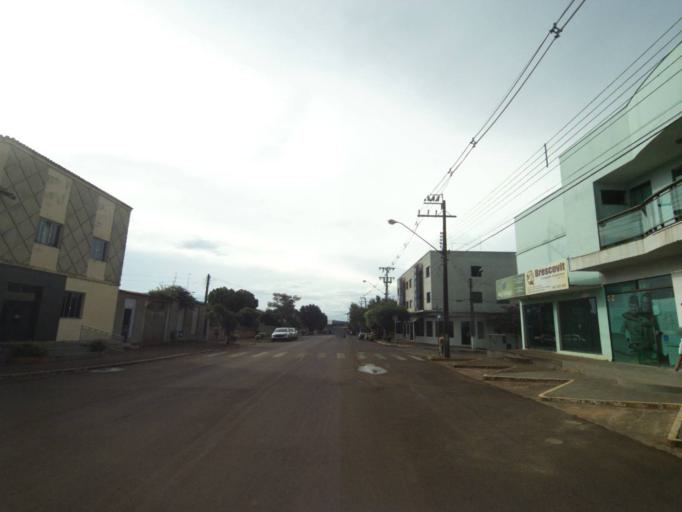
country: BR
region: Parana
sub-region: Guaraniacu
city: Guaraniacu
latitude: -25.0979
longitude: -52.8712
